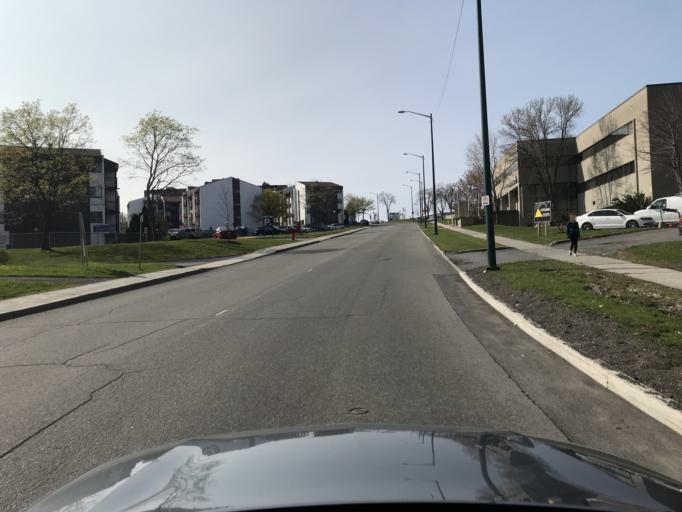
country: CA
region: Quebec
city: L'Ancienne-Lorette
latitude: 46.7892
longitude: -71.2821
